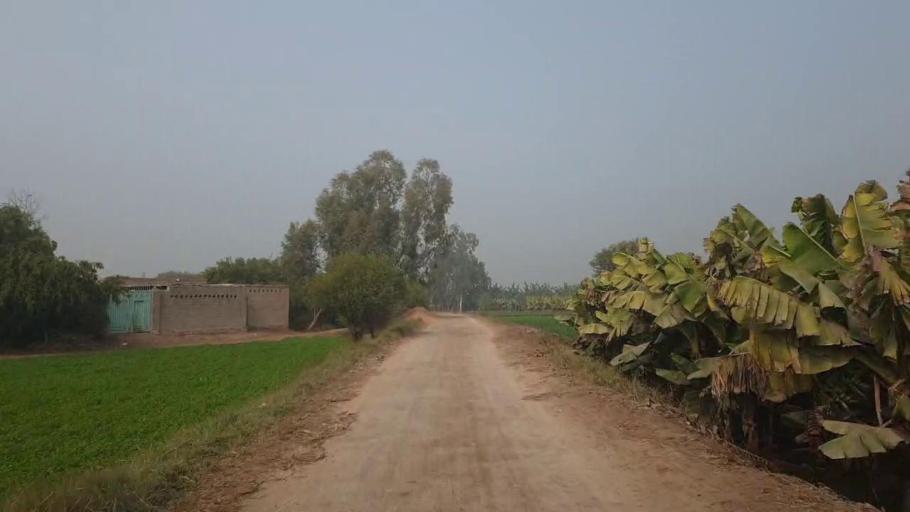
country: PK
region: Sindh
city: Bhit Shah
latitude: 25.8116
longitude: 68.5790
